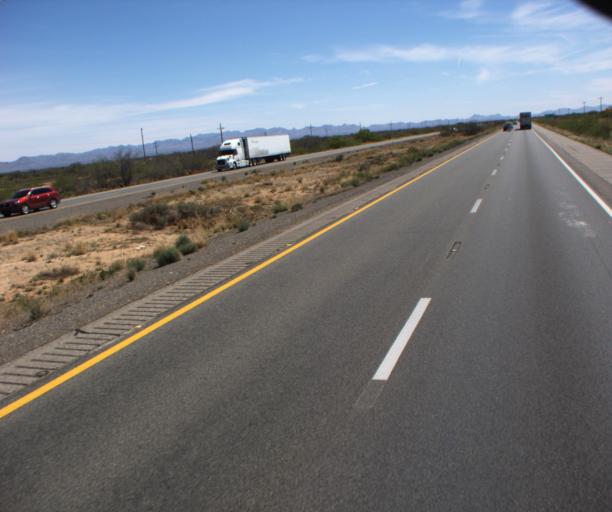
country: US
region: Arizona
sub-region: Cochise County
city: Willcox
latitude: 32.3123
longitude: -109.4205
